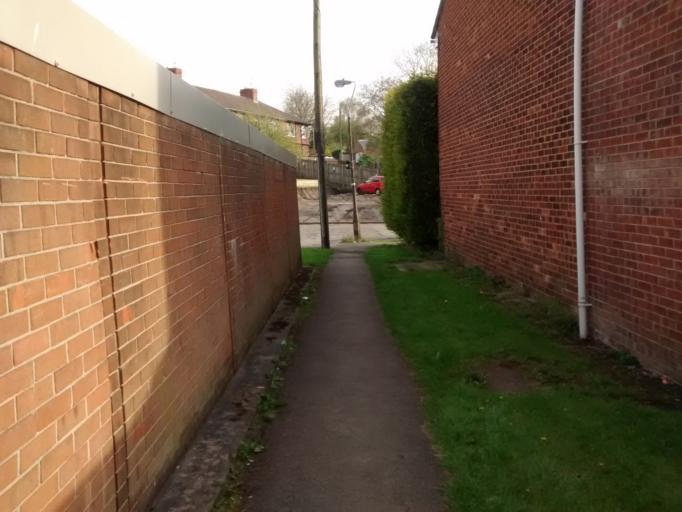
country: GB
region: England
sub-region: County Durham
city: Durham
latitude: 54.7714
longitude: -1.5683
